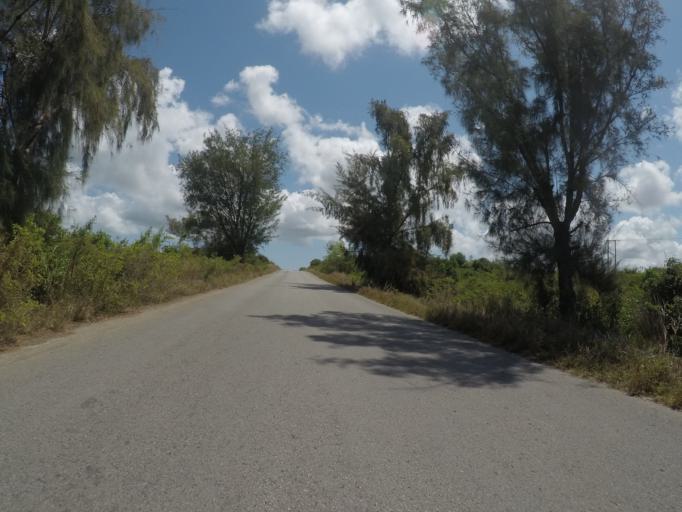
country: TZ
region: Zanzibar Central/South
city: Nganane
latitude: -6.2809
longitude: 39.4747
